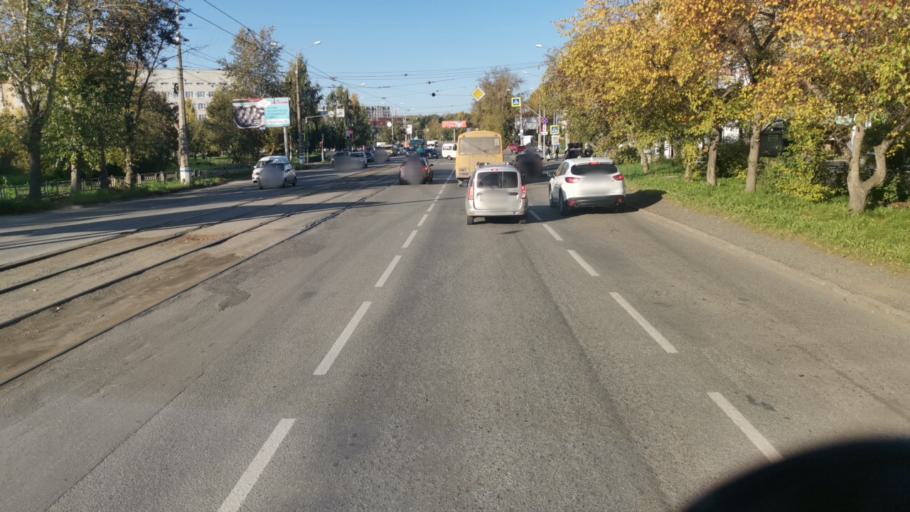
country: RU
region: Sverdlovsk
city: Nizhniy Tagil
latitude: 57.9099
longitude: 59.9471
